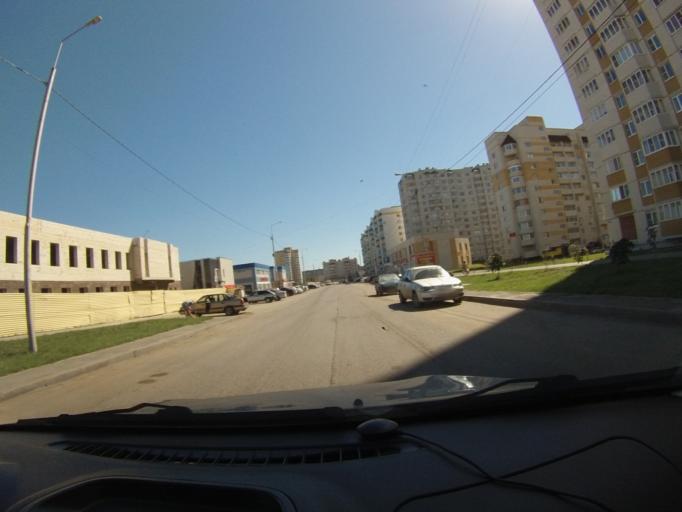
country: RU
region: Tambov
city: Tambov
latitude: 52.7717
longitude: 41.4029
